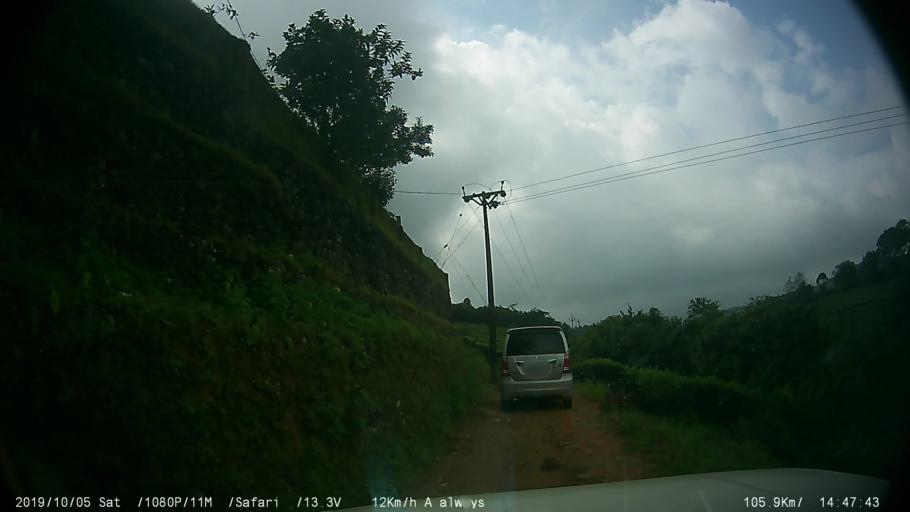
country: IN
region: Kerala
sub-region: Kottayam
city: Erattupetta
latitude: 9.6178
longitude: 76.9408
